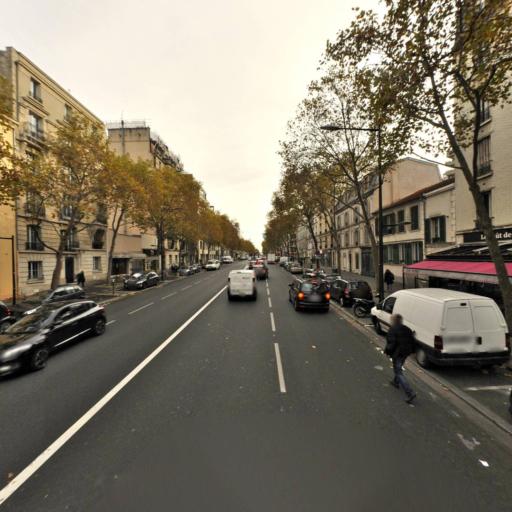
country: FR
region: Ile-de-France
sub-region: Departement des Hauts-de-Seine
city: Boulogne-Billancourt
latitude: 48.8396
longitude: 2.2413
